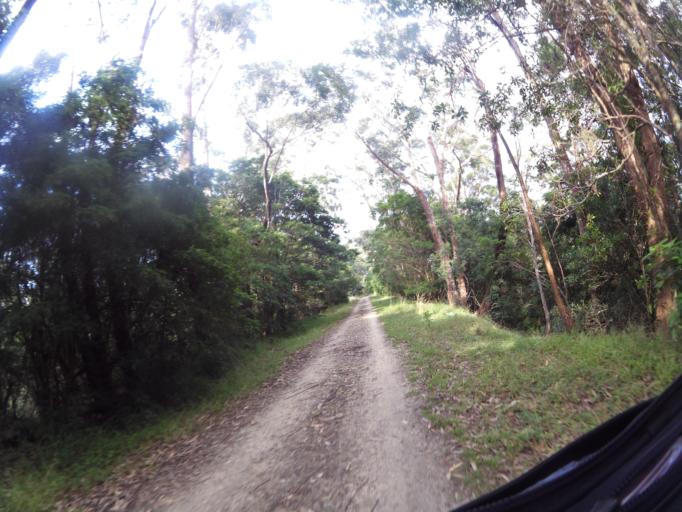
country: AU
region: Victoria
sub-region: East Gippsland
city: Lakes Entrance
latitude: -37.7262
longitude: 148.4282
